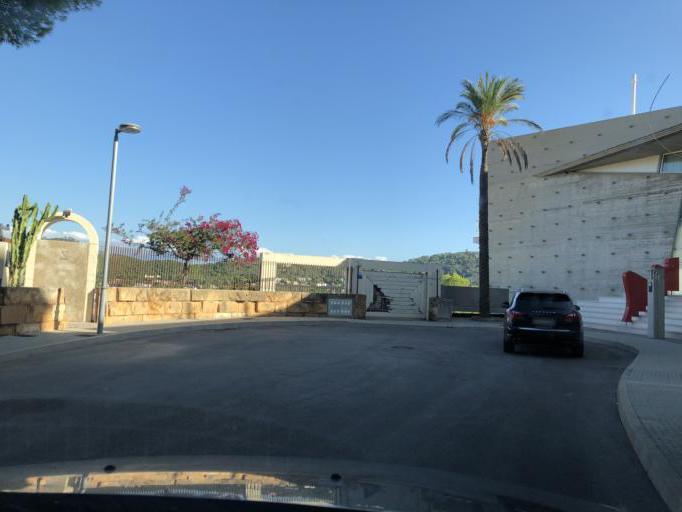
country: ES
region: Balearic Islands
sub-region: Illes Balears
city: Camp de Mar
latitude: 39.5381
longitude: 2.4118
